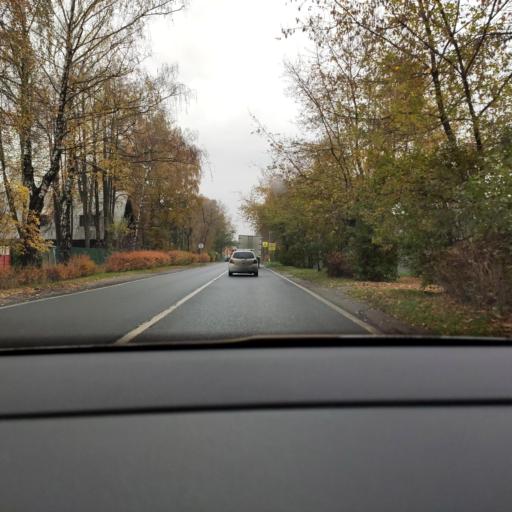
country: RU
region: Moskovskaya
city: Druzhba
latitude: 55.8854
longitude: 37.7465
